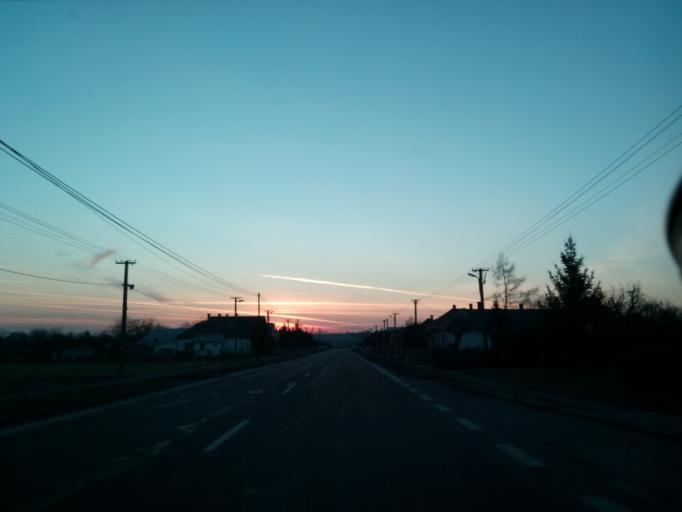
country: SK
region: Kosicky
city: Vinne
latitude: 48.7660
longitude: 22.0625
